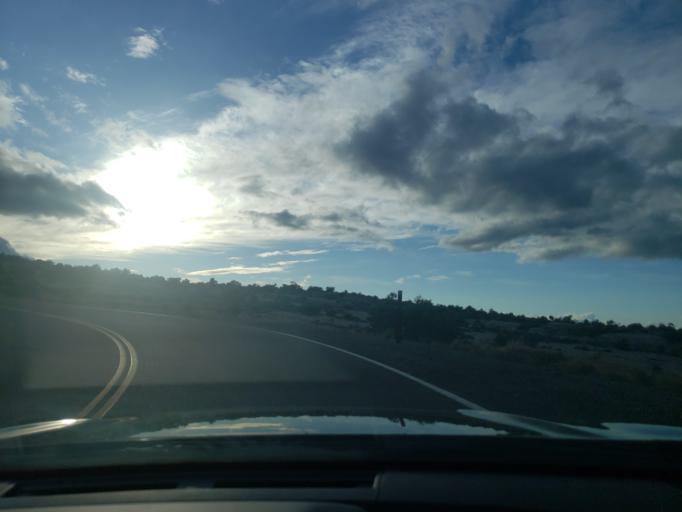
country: US
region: Colorado
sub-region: Mesa County
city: Redlands
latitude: 39.0351
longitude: -108.6459
